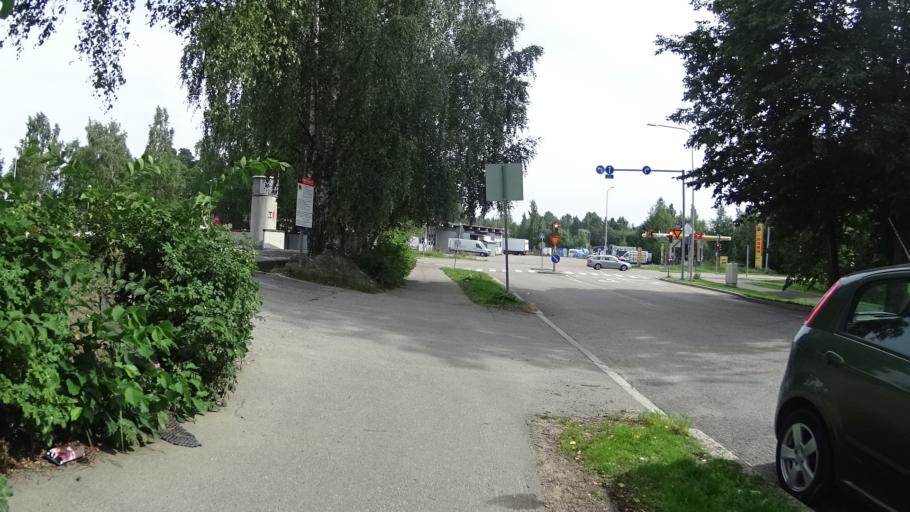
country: FI
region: Uusimaa
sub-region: Helsinki
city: Teekkarikylae
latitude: 60.2252
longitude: 24.8488
